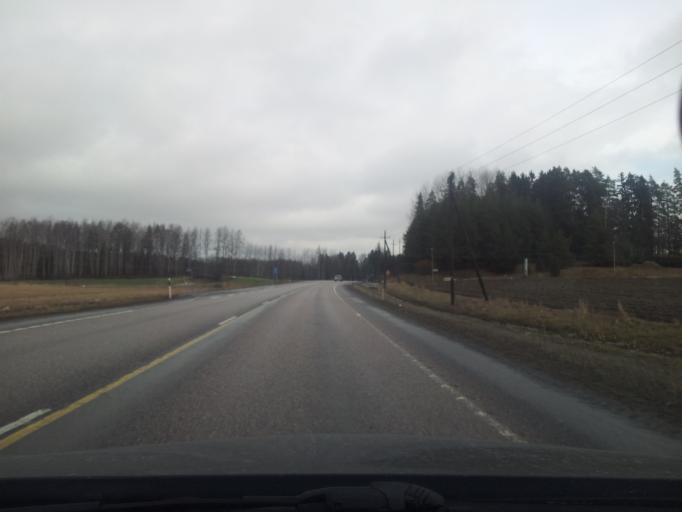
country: FI
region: Uusimaa
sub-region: Helsinki
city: Espoo
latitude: 60.1674
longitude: 24.5479
